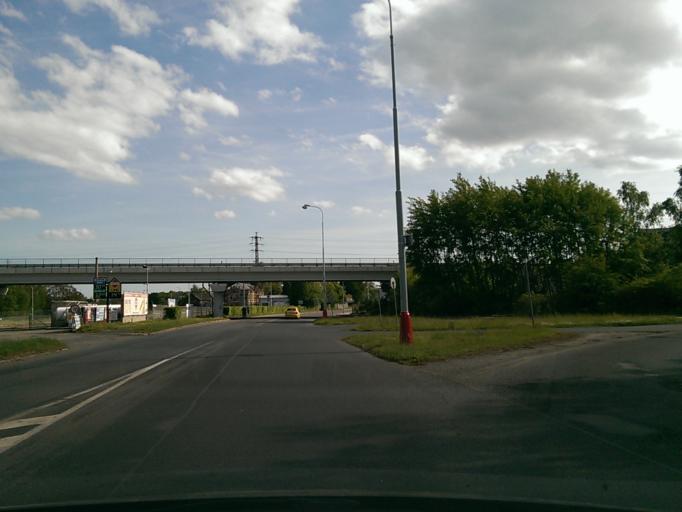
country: CZ
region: Central Bohemia
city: Mnichovo Hradiste
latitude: 50.5154
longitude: 14.9725
